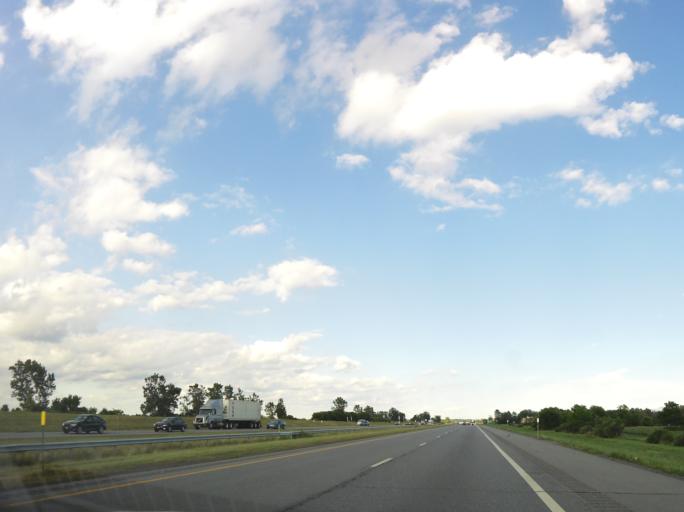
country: US
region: New York
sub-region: Erie County
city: Harris Hill
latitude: 42.9472
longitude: -78.6671
